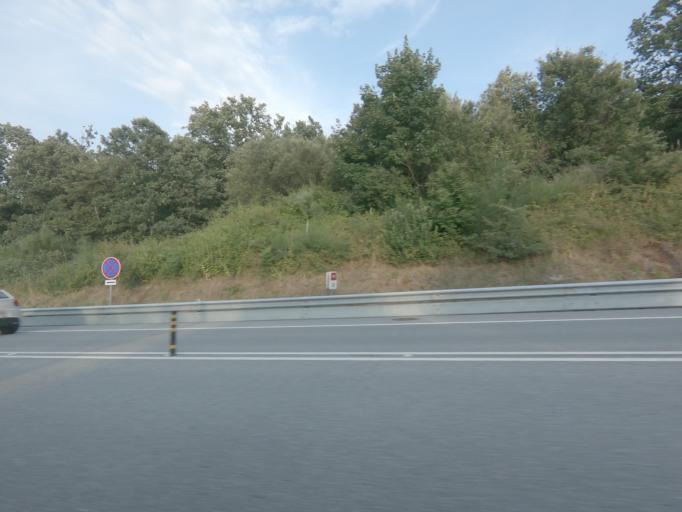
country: PT
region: Vila Real
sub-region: Vila Real
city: Vila Real
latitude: 41.2813
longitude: -7.7669
